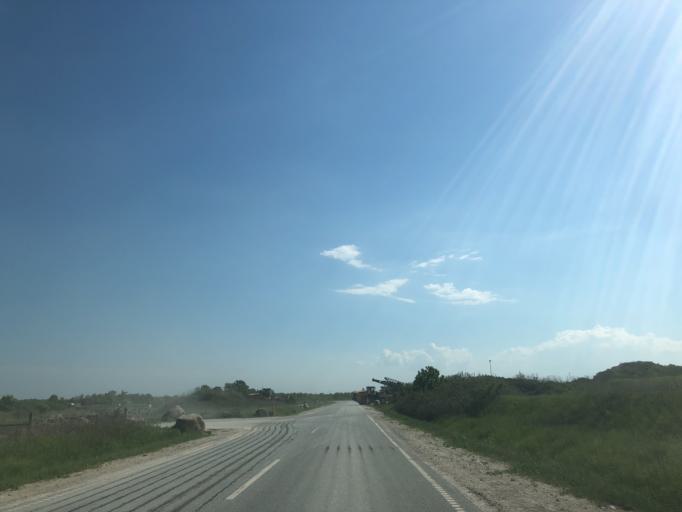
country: DK
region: Zealand
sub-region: Roskilde Kommune
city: Vindinge
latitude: 55.6214
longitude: 12.1210
